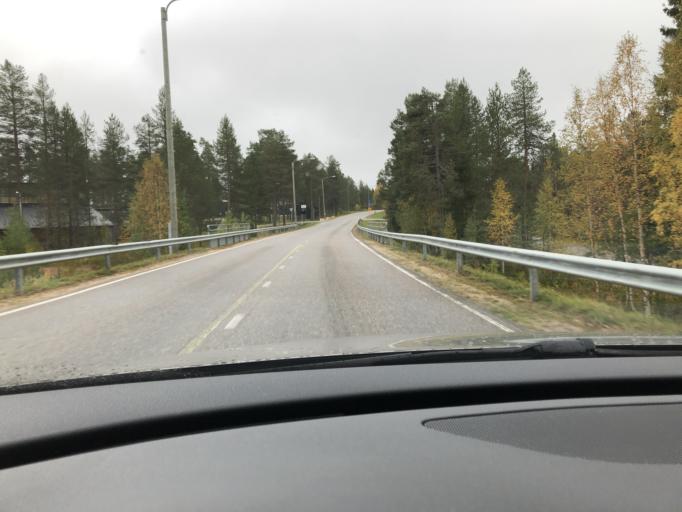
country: FI
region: Lapland
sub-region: Itae-Lappi
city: Posio
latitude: 66.1148
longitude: 28.1823
